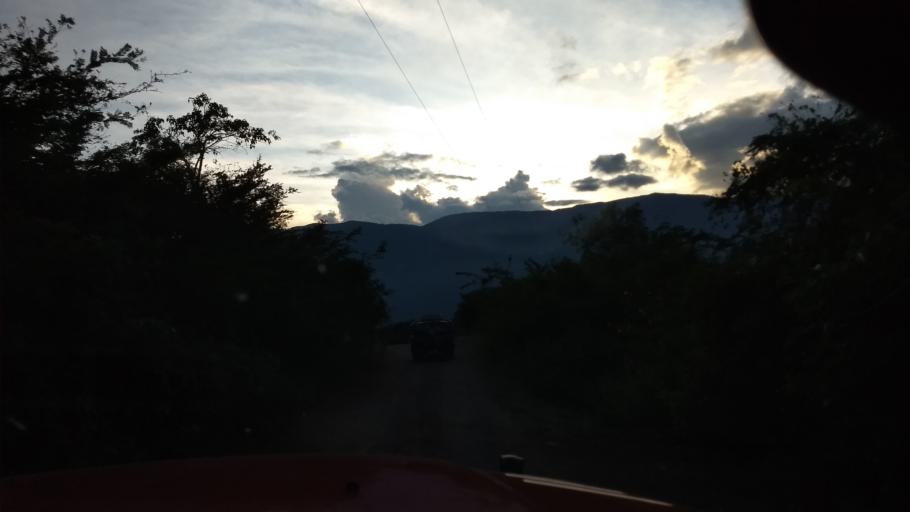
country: MX
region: Colima
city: Suchitlan
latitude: 19.4795
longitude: -103.8020
